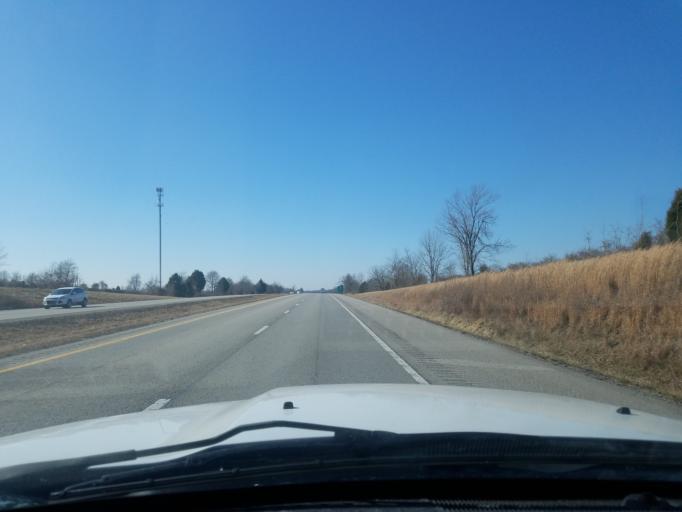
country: US
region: Kentucky
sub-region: Grayson County
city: Leitchfield
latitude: 37.4951
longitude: -86.1842
